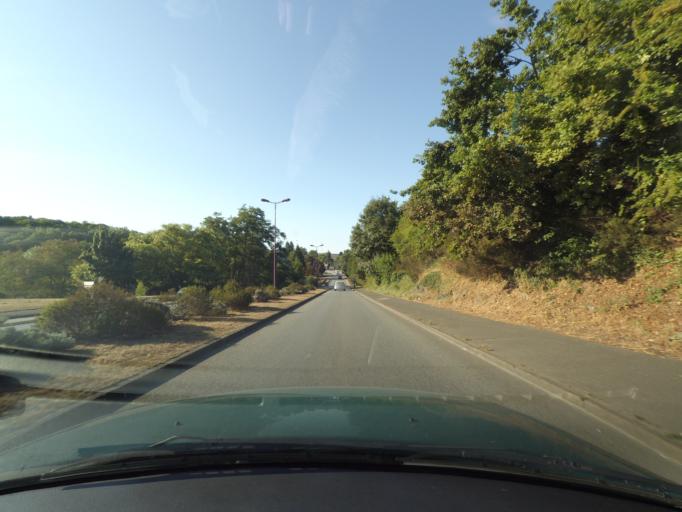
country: FR
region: Poitou-Charentes
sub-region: Departement des Deux-Sevres
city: Chatillon-sur-Thouet
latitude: 46.6583
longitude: -0.2398
